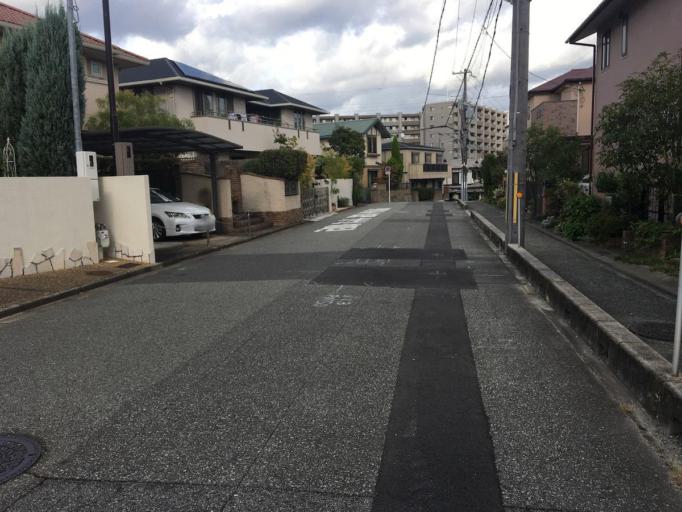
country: JP
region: Osaka
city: Suita
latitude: 34.7994
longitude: 135.5185
